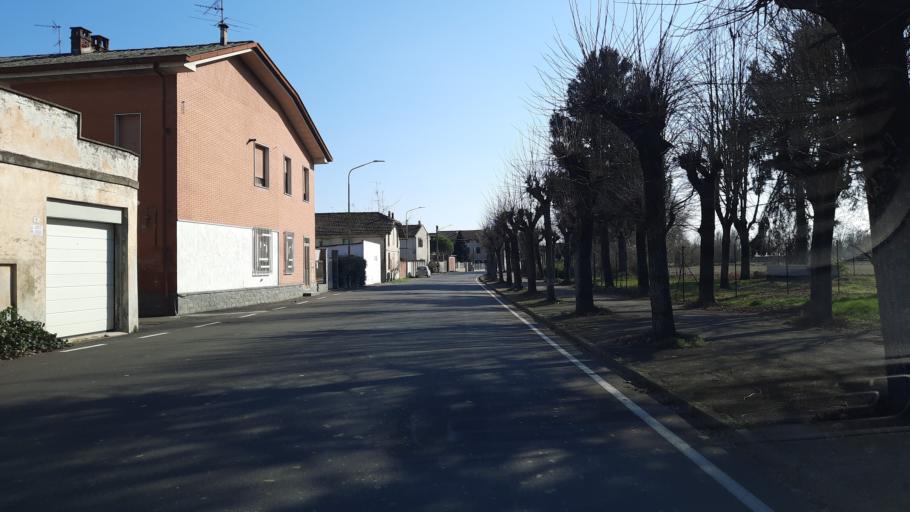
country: IT
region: Piedmont
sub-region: Provincia di Vercelli
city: Costanzana
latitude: 45.2347
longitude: 8.3702
